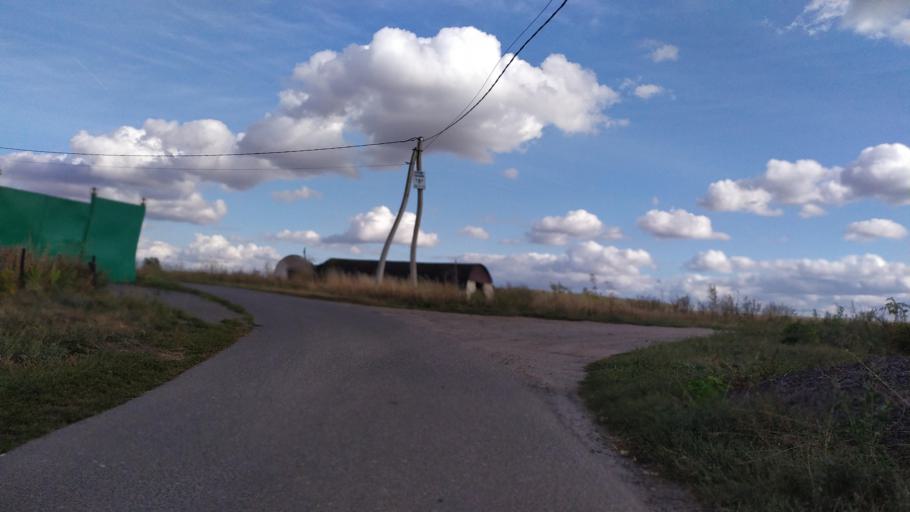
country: RU
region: Kursk
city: Kursk
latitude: 51.6276
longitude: 36.1547
